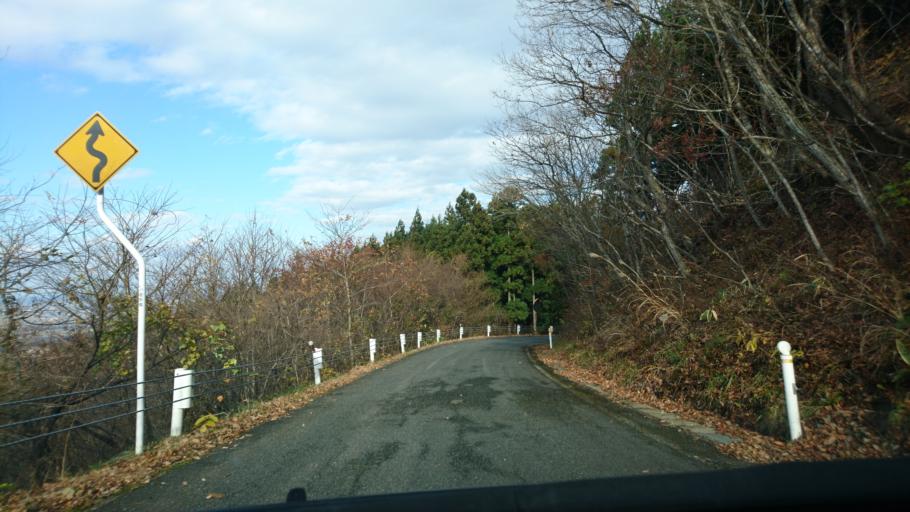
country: JP
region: Iwate
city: Ichinoseki
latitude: 39.0210
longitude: 141.1761
